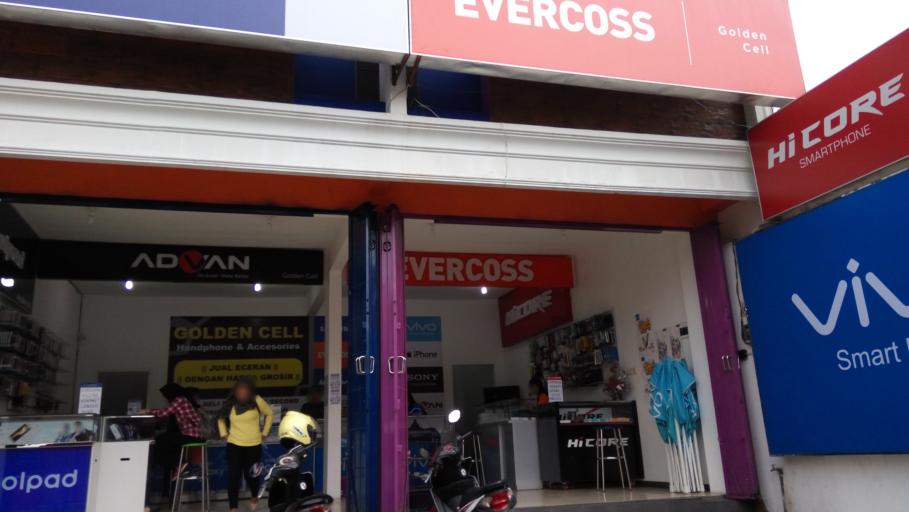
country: ID
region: East Java
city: Malang
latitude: -7.9468
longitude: 112.6090
